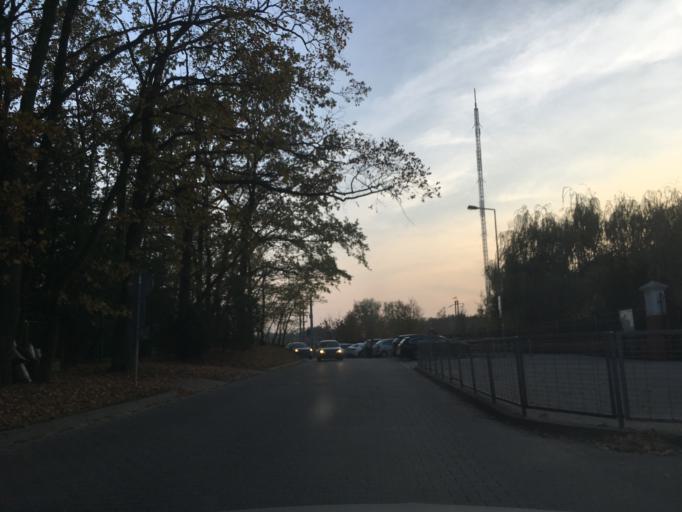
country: PL
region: Masovian Voivodeship
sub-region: Powiat piaseczynski
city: Lesznowola
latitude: 52.0774
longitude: 20.8915
